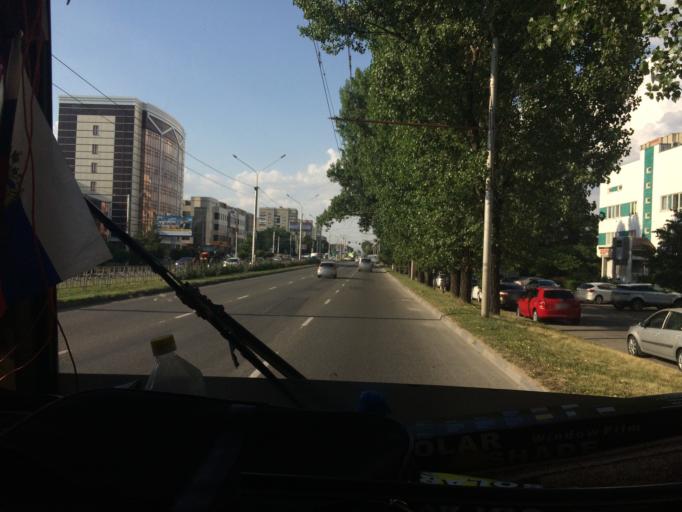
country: RU
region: Stavropol'skiy
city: Stavropol'
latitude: 45.0169
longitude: 41.9320
